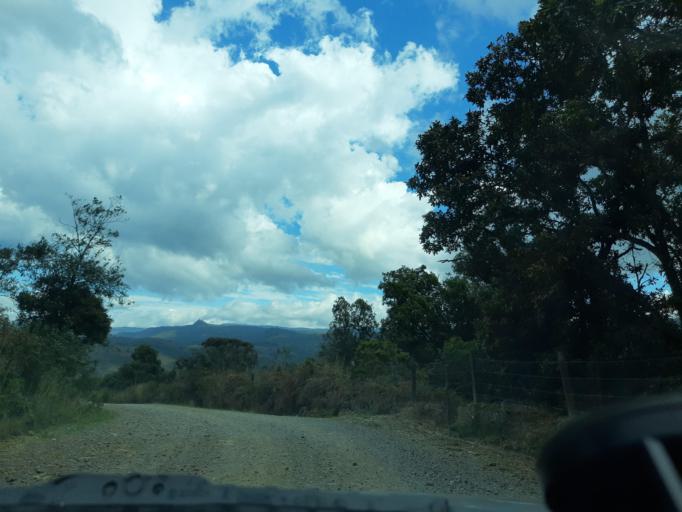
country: CO
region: Boyaca
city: Raquira
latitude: 5.5057
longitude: -73.6713
